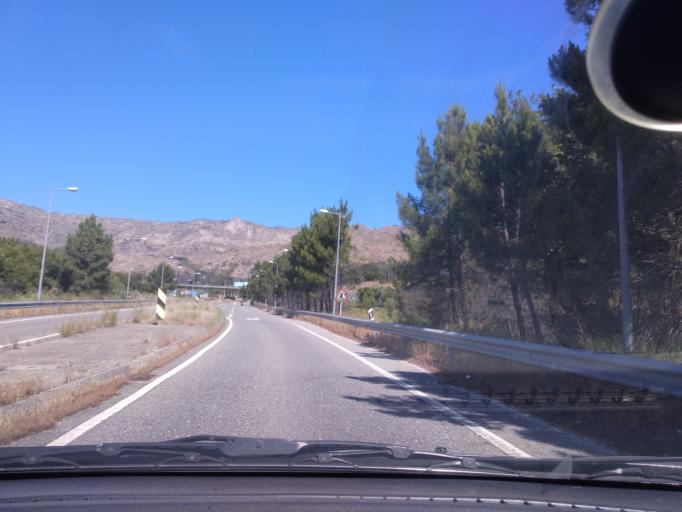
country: PT
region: Castelo Branco
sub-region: Concelho do Fundao
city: Fundao
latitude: 40.0754
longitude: -7.4744
